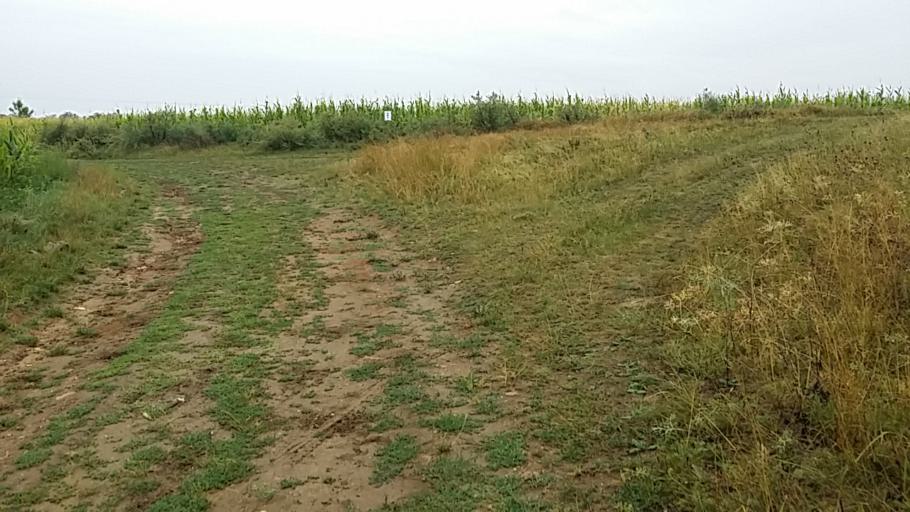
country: HU
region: Pest
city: Pecel
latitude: 47.4779
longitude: 19.3176
